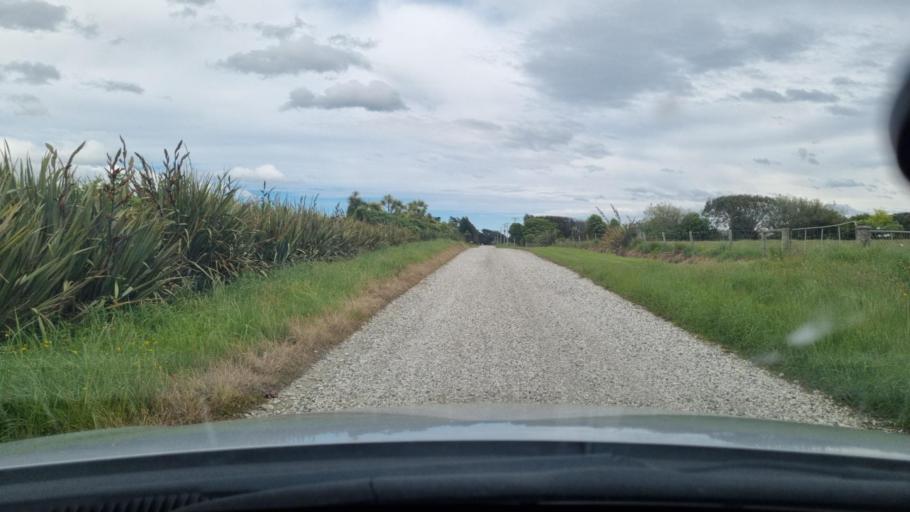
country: NZ
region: Southland
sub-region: Invercargill City
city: Invercargill
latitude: -46.4036
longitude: 168.2586
